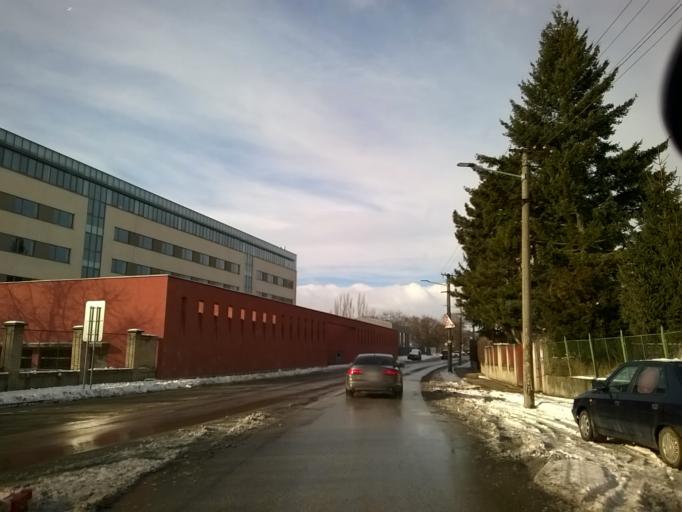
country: SK
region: Nitriansky
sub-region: Okres Nitra
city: Nitra
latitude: 48.3232
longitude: 18.0943
